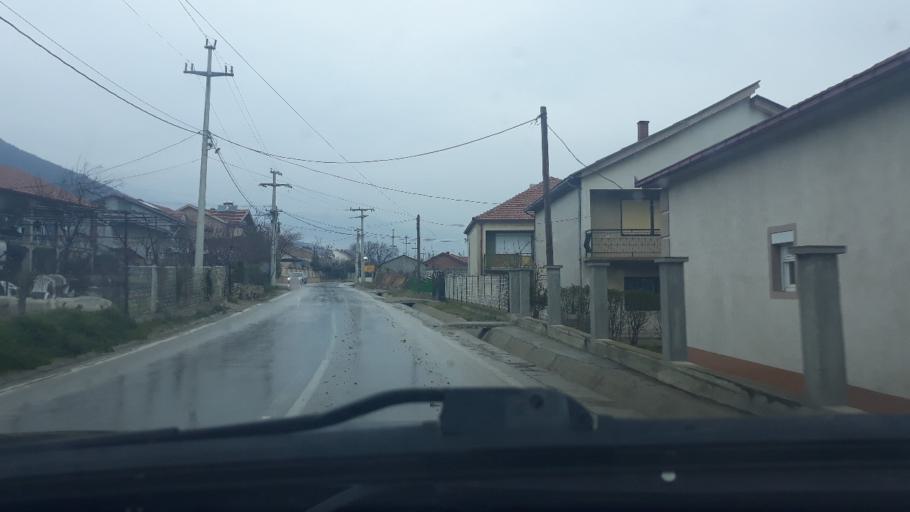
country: MK
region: Dojran
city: Star Dojran
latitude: 41.2601
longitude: 22.7428
